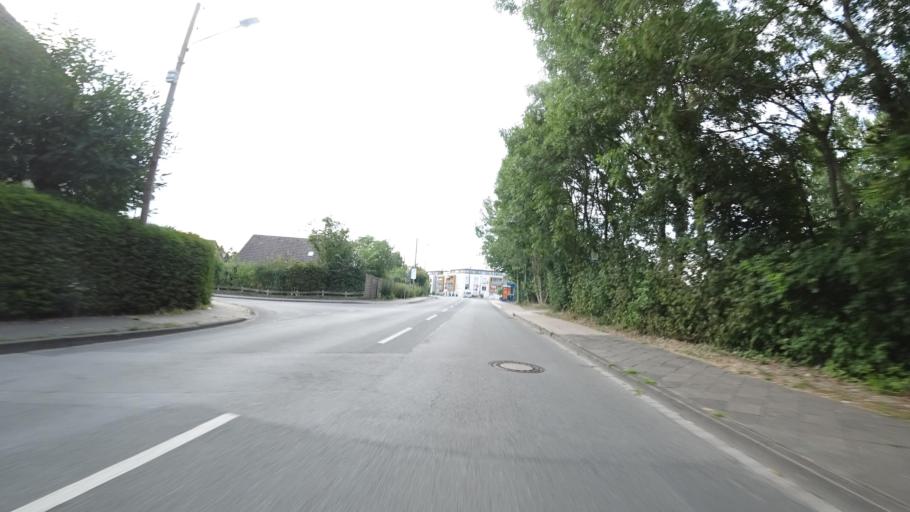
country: DE
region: North Rhine-Westphalia
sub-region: Regierungsbezirk Detmold
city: Steinhagen
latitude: 51.9700
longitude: 8.4662
